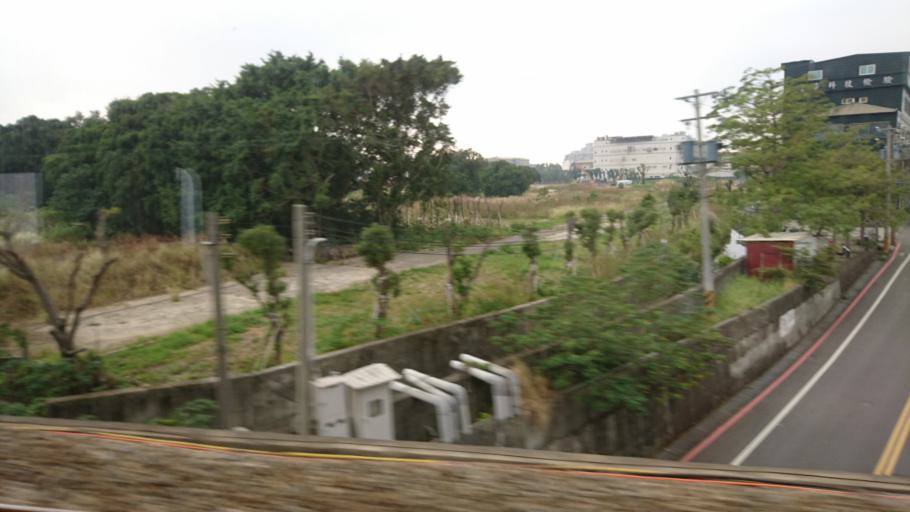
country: TW
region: Taiwan
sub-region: Hsinchu
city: Zhubei
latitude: 24.8459
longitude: 121.0136
